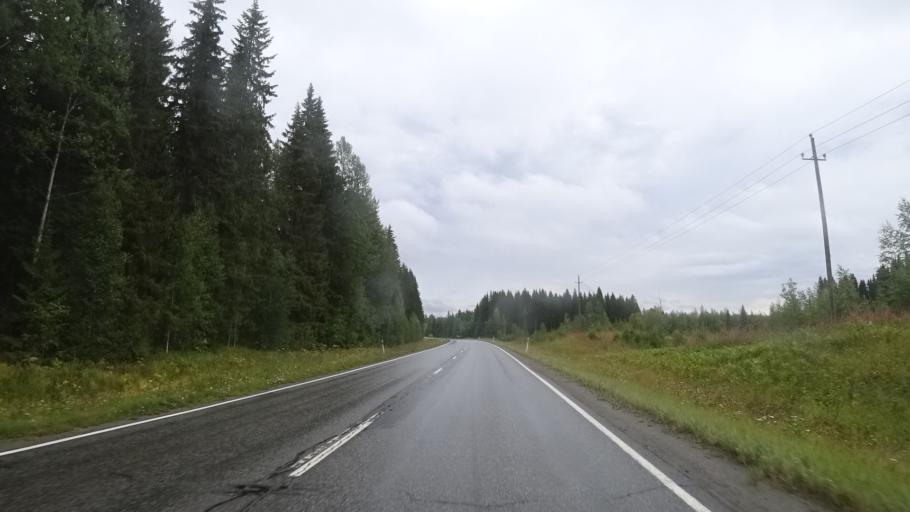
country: FI
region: Southern Savonia
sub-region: Savonlinna
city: Kerimaeki
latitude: 61.9860
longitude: 29.2843
